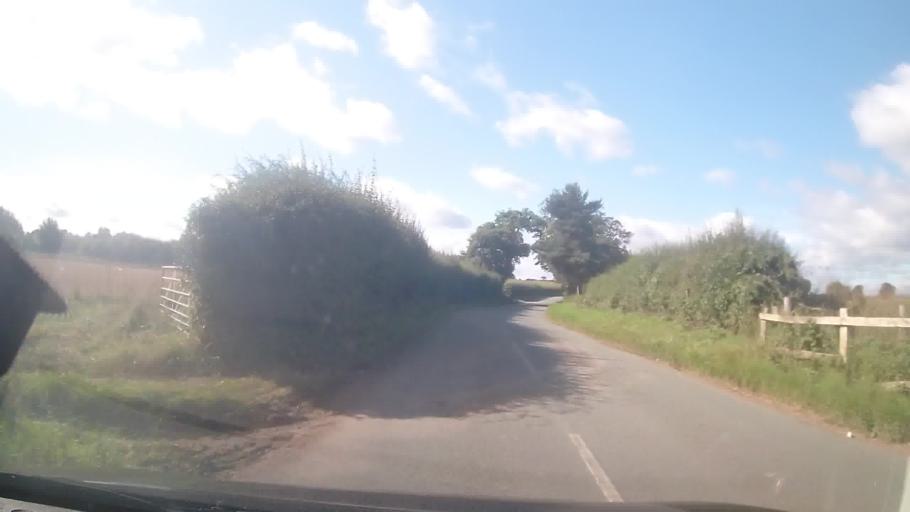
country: GB
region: England
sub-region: Shropshire
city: Ford
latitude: 52.7221
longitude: -2.8382
